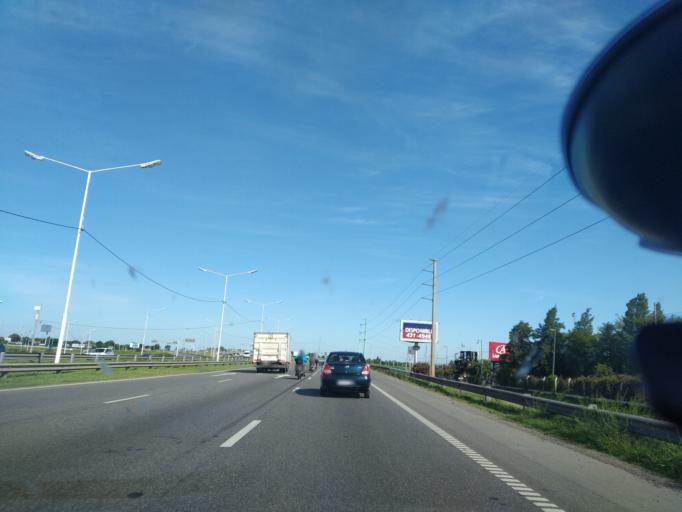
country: AR
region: Santa Fe
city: Gobernador Galvez
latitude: -33.0127
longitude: -60.6692
